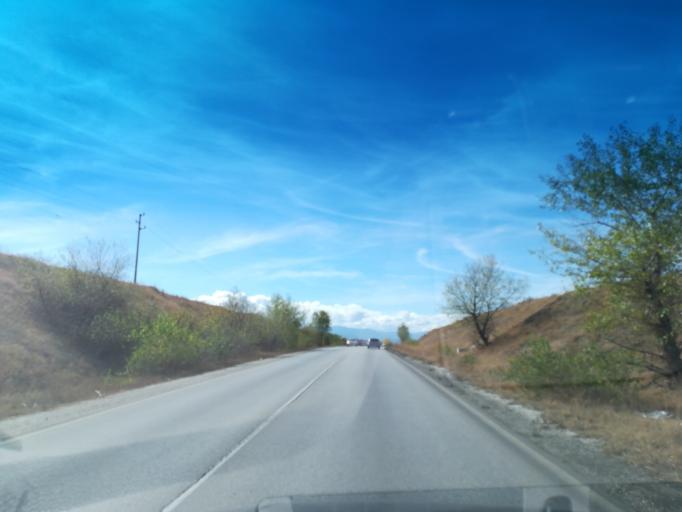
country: BG
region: Plovdiv
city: Stamboliyski
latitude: 42.1305
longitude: 24.6048
